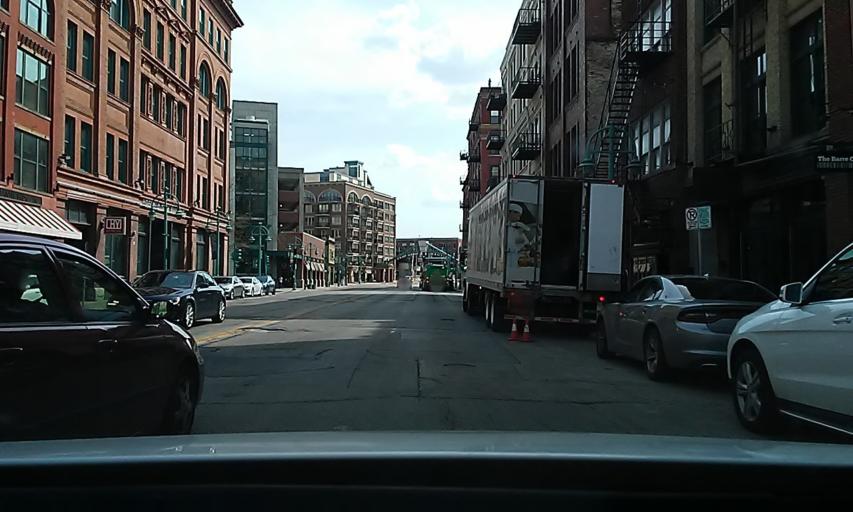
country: US
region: Wisconsin
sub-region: Milwaukee County
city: Milwaukee
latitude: 43.0333
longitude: -87.9093
